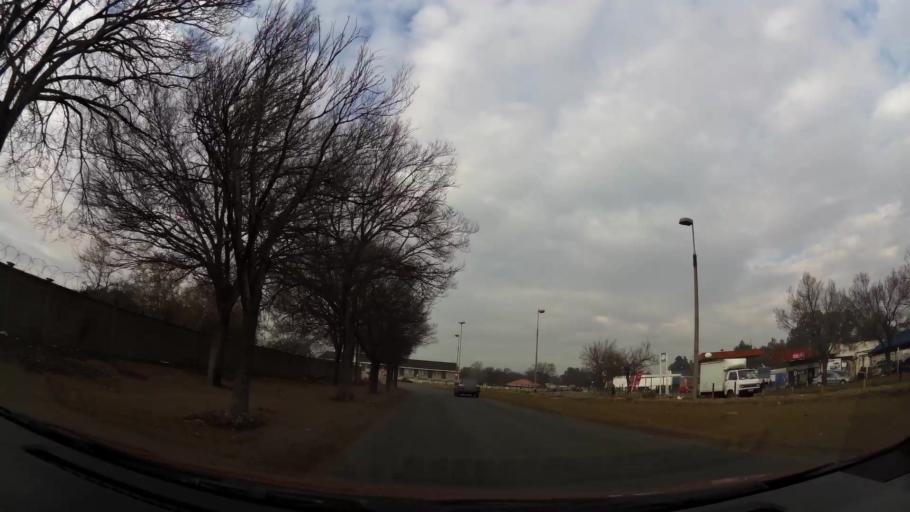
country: ZA
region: Gauteng
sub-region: Sedibeng District Municipality
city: Vanderbijlpark
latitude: -26.6909
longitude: 27.8132
